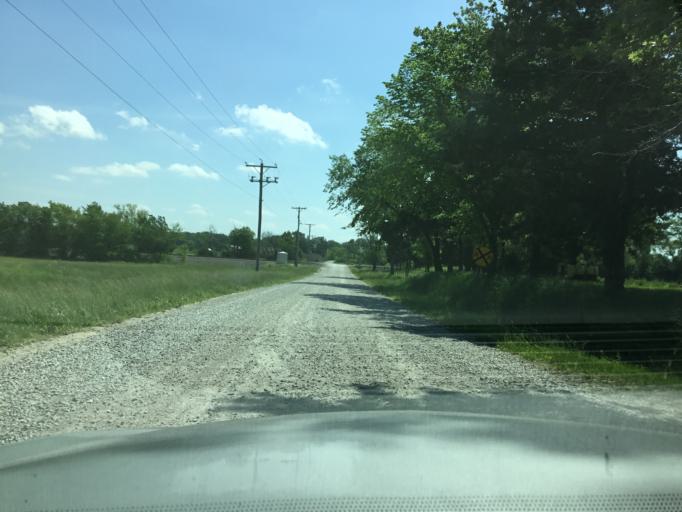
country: US
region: Kansas
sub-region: Labette County
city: Parsons
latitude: 37.3110
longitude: -95.2522
